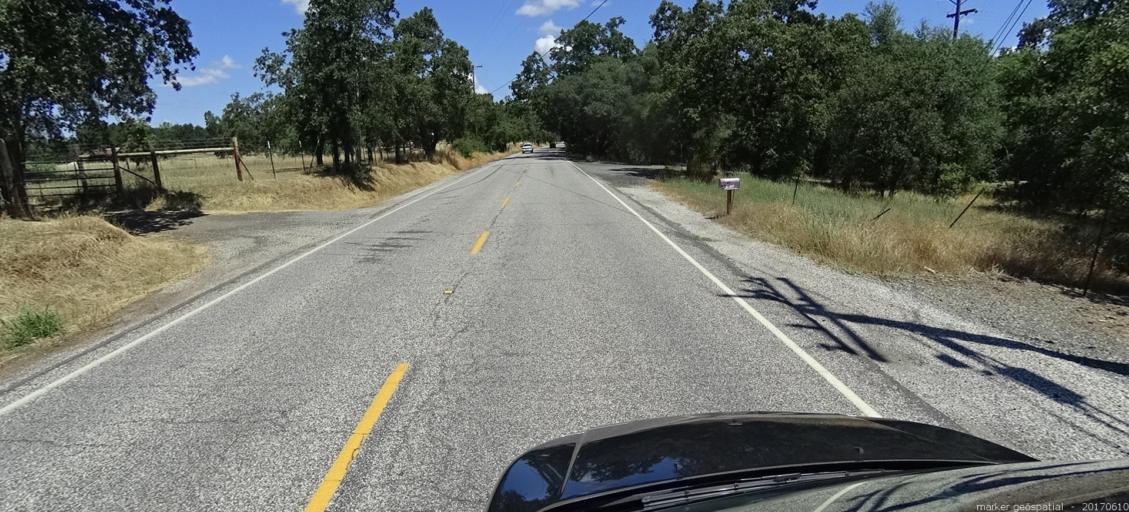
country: US
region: California
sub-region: Butte County
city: Oroville East
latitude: 39.4697
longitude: -121.4591
